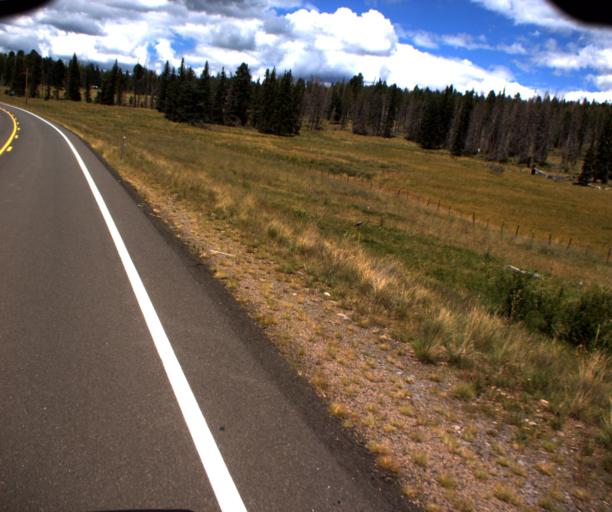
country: US
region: Arizona
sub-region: Apache County
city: Eagar
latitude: 33.9294
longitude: -109.4669
